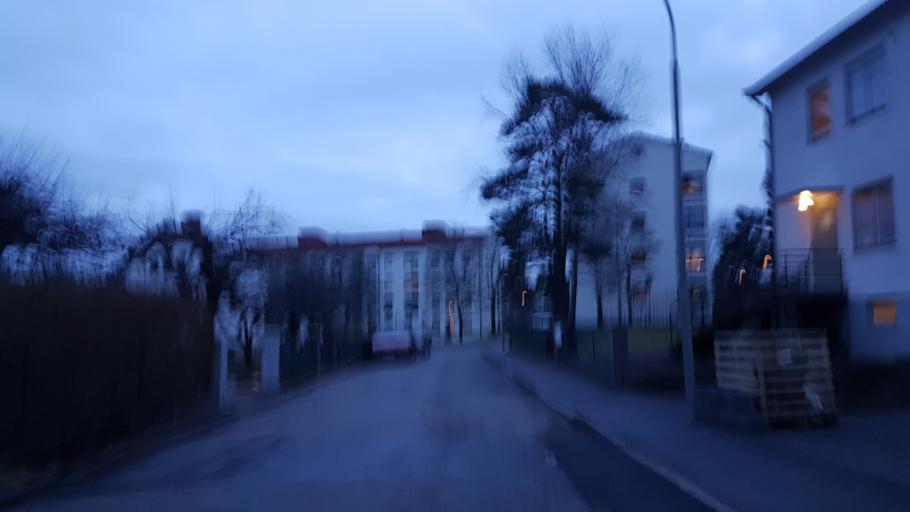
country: SE
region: Stockholm
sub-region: Stockholms Kommun
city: Arsta
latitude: 59.2755
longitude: 18.0521
